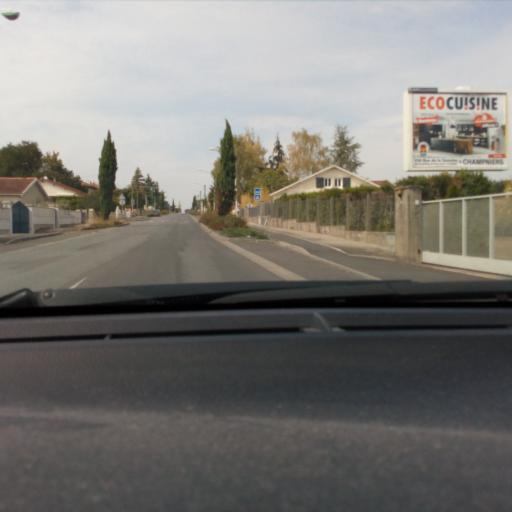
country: FR
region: Poitou-Charentes
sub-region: Departement de la Charente
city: Saint-Yrieix-sur-Charente
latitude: 45.6745
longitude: 0.1241
